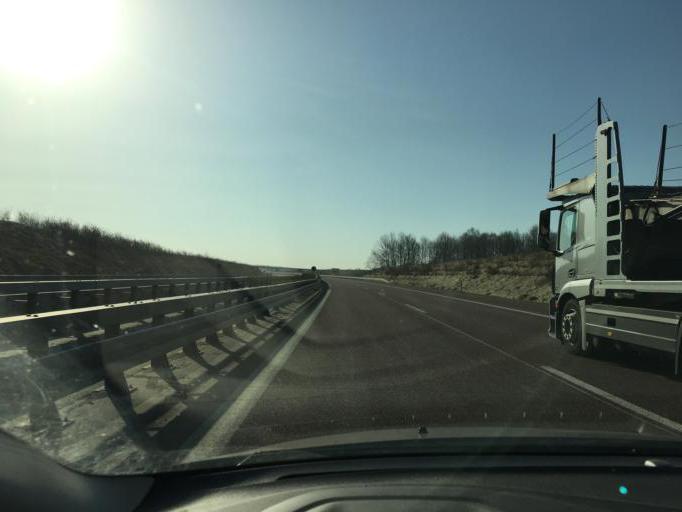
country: DE
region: Saxony
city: Niederfrohna
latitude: 50.9132
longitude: 12.7020
